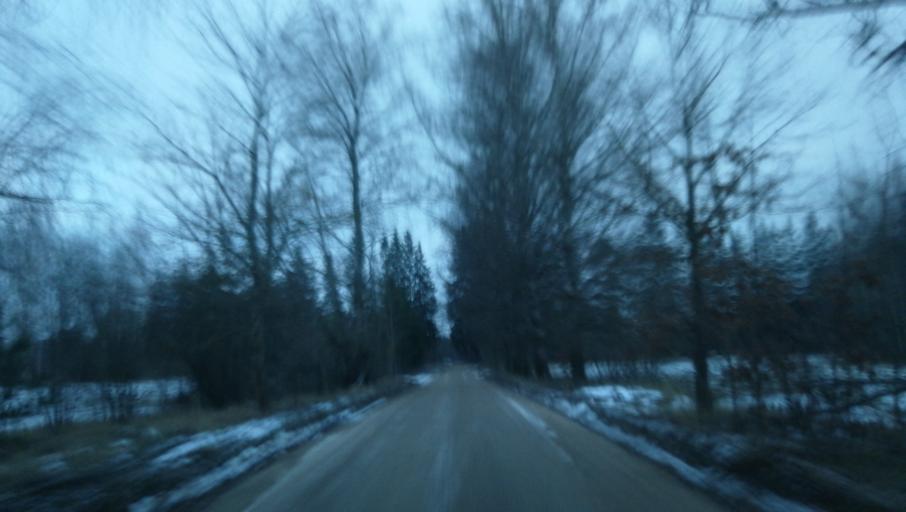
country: LV
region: Garkalne
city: Garkalne
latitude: 57.0177
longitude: 24.3866
